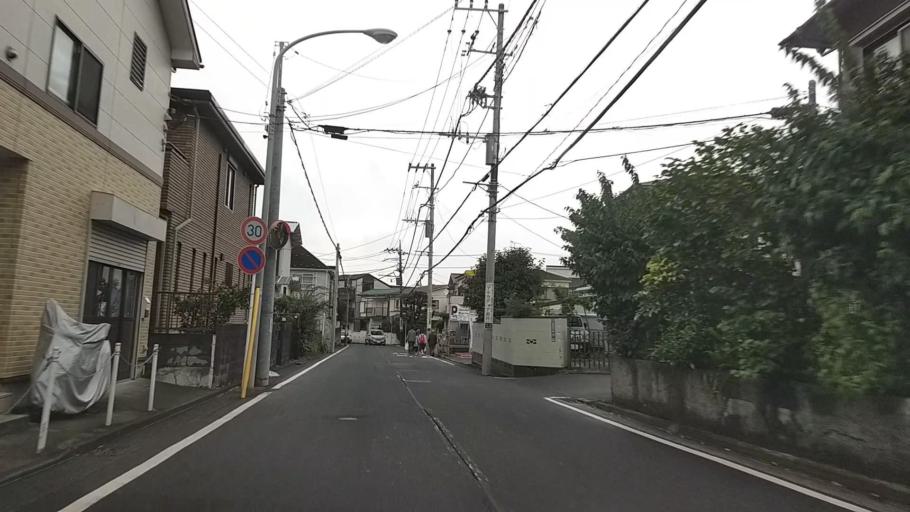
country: JP
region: Kanagawa
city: Yokohama
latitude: 35.4148
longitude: 139.6027
